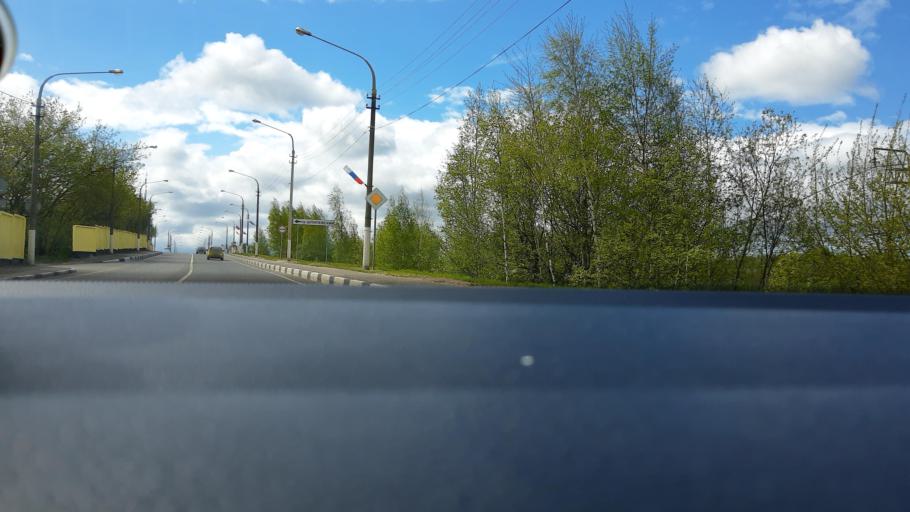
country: RU
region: Moskovskaya
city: Dmitrov
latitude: 56.3301
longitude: 37.5030
